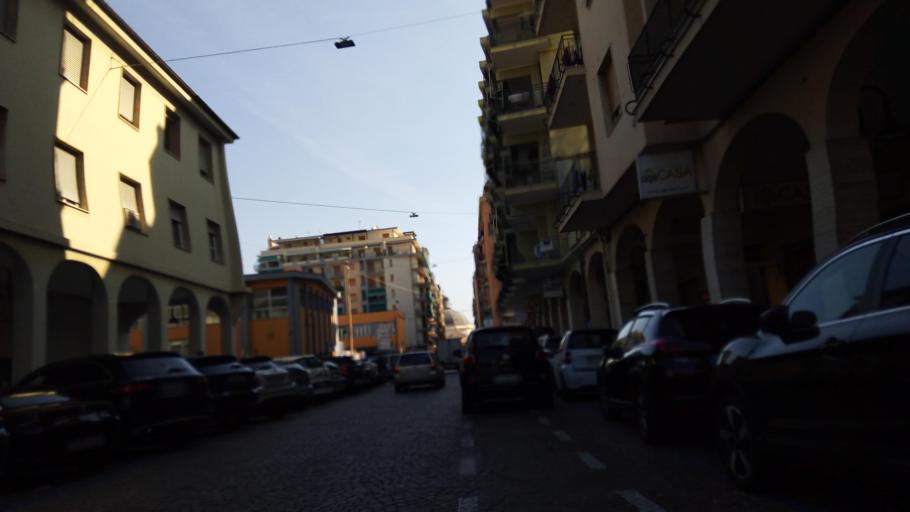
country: IT
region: Liguria
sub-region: Provincia di Savona
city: Loano
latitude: 44.1256
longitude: 8.2570
